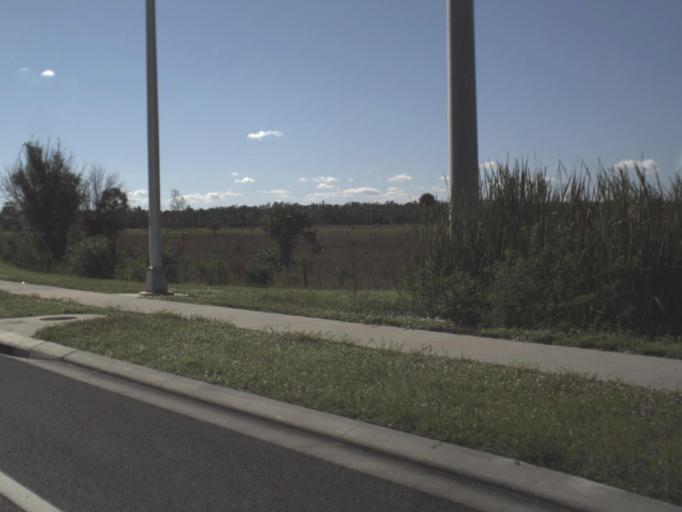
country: US
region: Florida
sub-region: Lee County
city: Gateway
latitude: 26.6218
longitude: -81.7717
